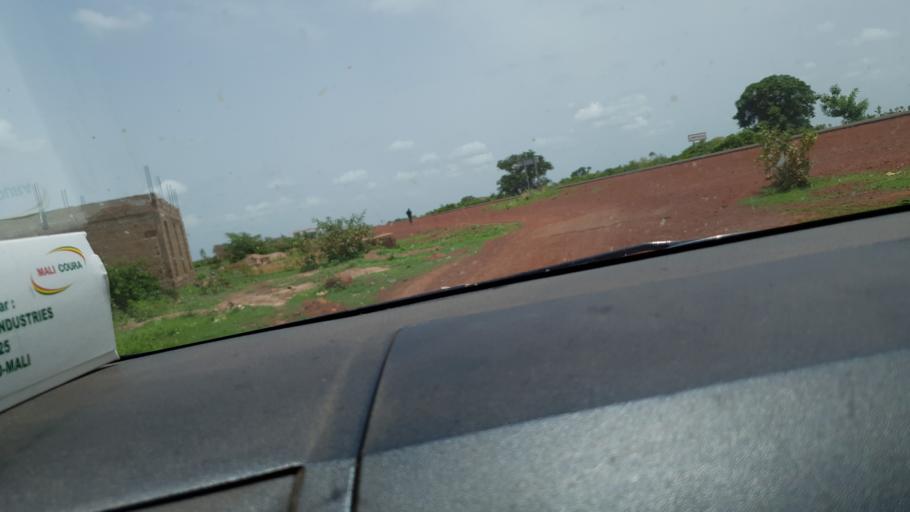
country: ML
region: Koulikoro
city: Koulikoro
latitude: 12.7114
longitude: -7.4249
